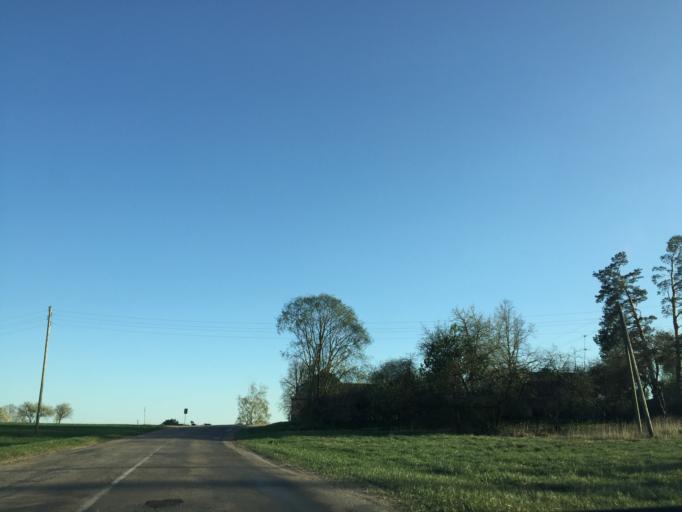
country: LV
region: Koknese
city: Koknese
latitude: 56.7105
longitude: 25.4935
